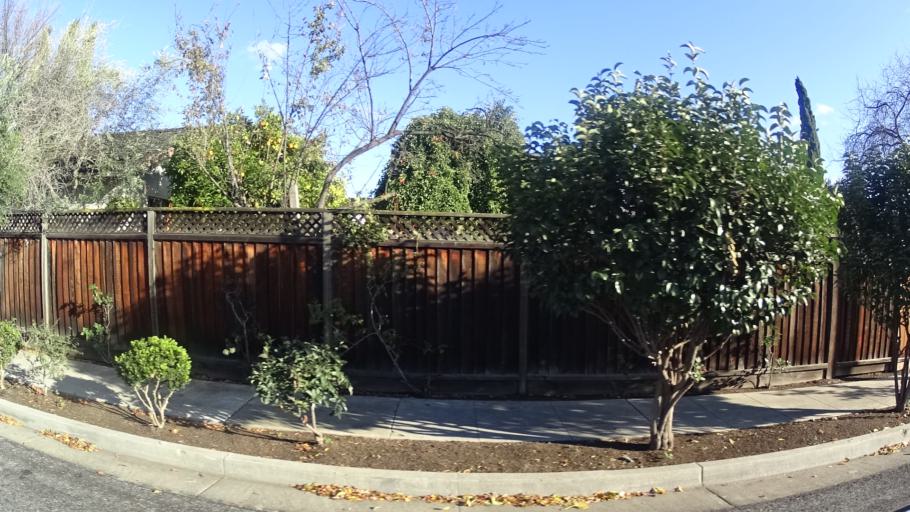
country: US
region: California
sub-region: Santa Clara County
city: Sunnyvale
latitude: 37.3790
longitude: -122.0421
